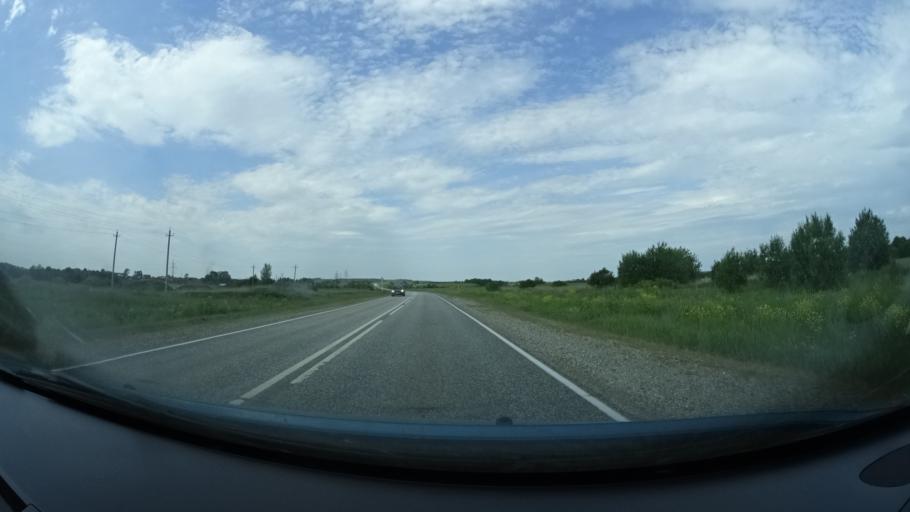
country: RU
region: Perm
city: Barda
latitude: 57.0833
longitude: 55.5421
